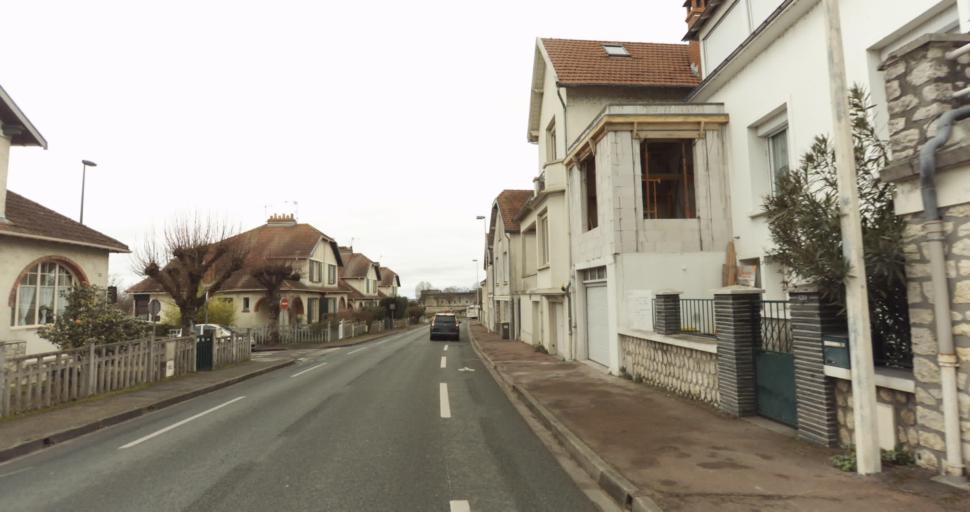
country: FR
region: Pays de la Loire
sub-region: Departement de Maine-et-Loire
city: Saumur
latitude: 47.2546
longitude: -0.0713
